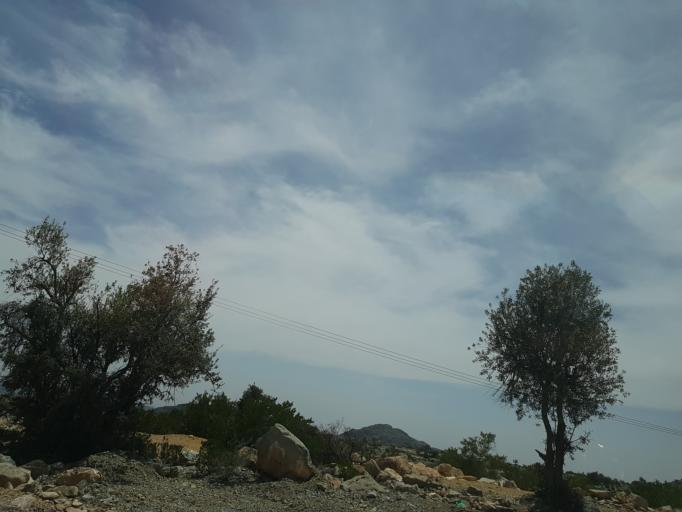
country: OM
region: Muhafazat ad Dakhiliyah
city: Nizwa
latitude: 23.1191
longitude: 57.6336
